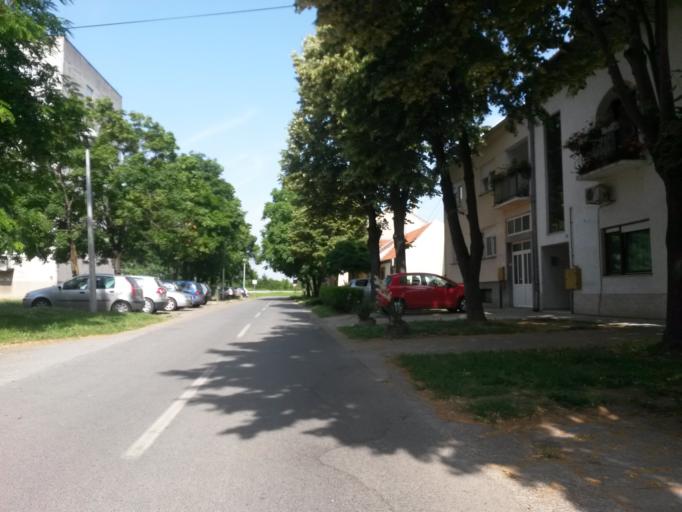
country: HR
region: Osjecko-Baranjska
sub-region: Grad Osijek
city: Osijek
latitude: 45.5472
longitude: 18.6743
